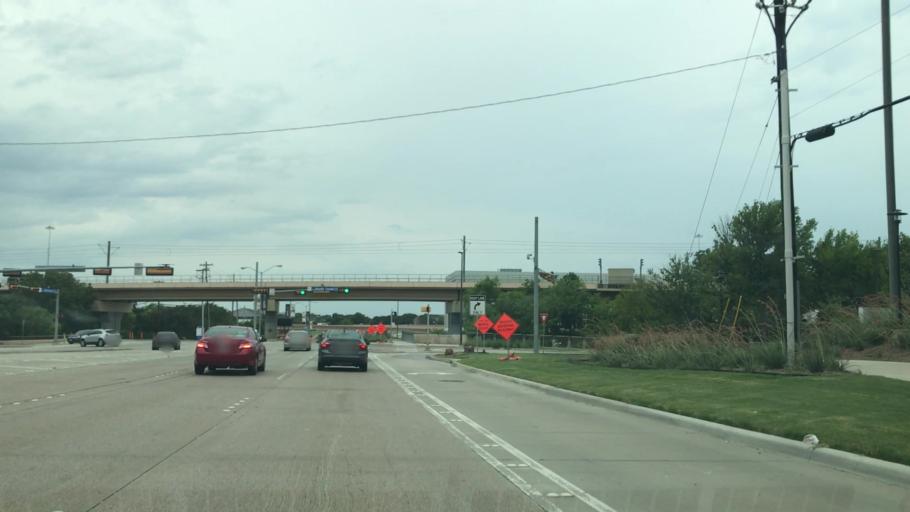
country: US
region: Texas
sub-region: Collin County
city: Plano
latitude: 32.9973
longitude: -96.7040
